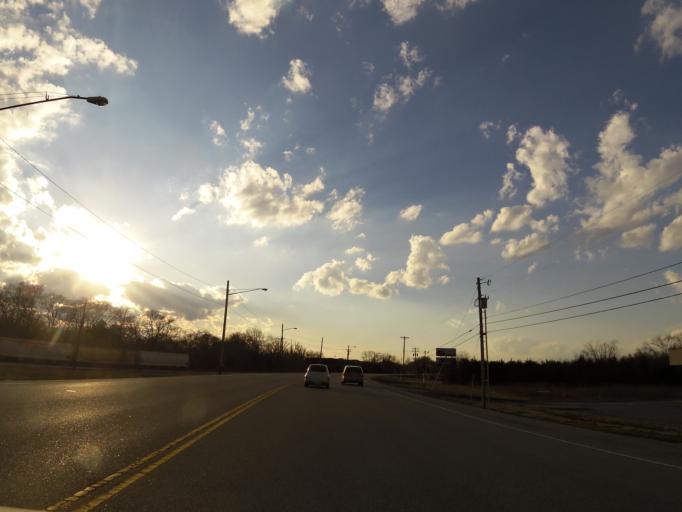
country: US
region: Tennessee
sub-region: Wilson County
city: Lebanon
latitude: 36.2133
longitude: -86.2979
